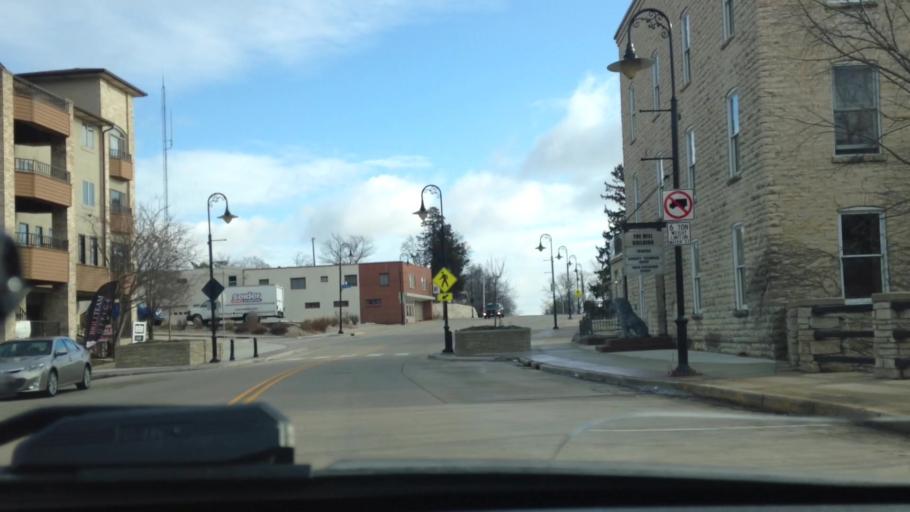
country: US
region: Wisconsin
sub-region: Waukesha County
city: Menomonee Falls
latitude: 43.1793
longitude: -88.1144
